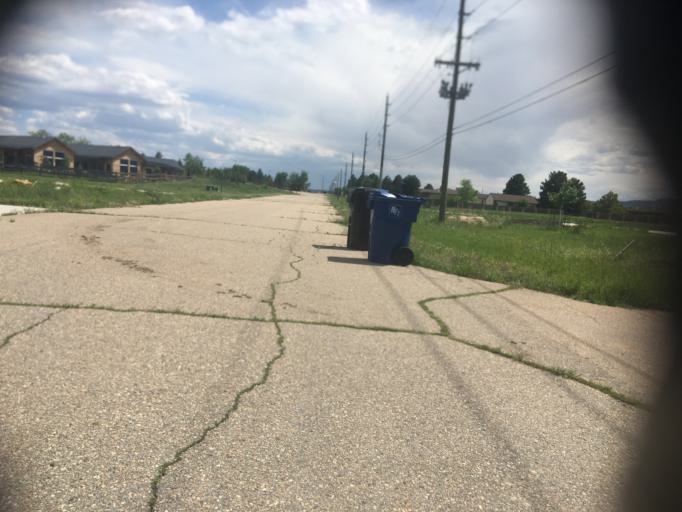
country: US
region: Colorado
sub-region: Boulder County
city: Superior
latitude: 39.9861
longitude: -105.1660
